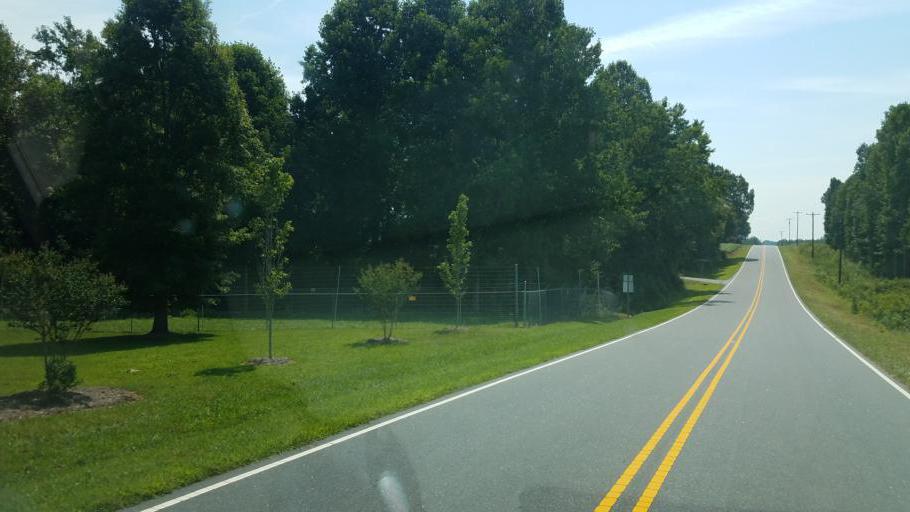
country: US
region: North Carolina
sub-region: Burke County
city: Icard
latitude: 35.5353
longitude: -81.5076
